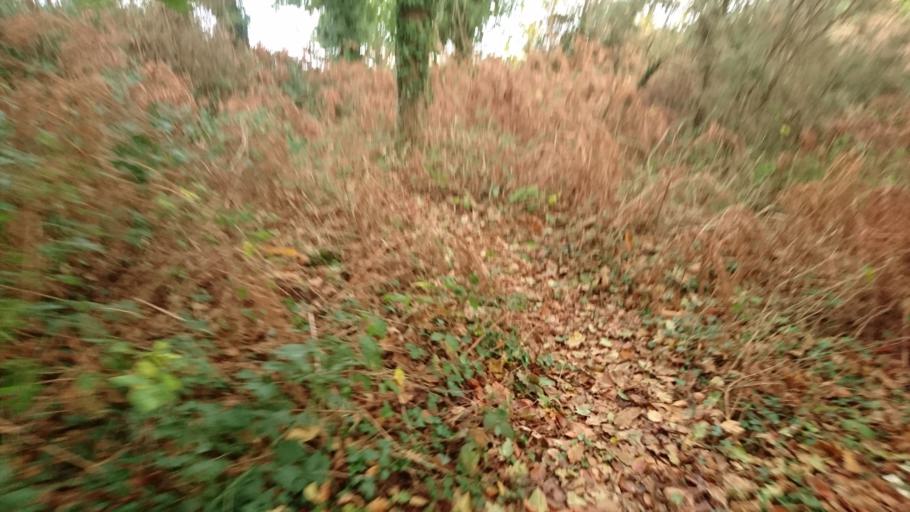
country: FR
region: Brittany
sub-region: Departement du Finistere
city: Lampaul-Plouarzel
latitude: 48.4364
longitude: -4.7676
